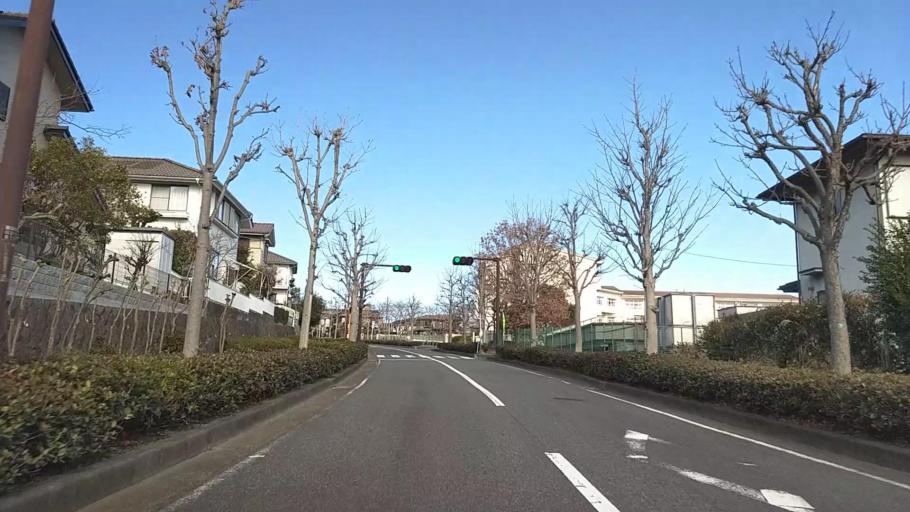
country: JP
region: Kanagawa
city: Isehara
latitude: 35.4436
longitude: 139.3059
